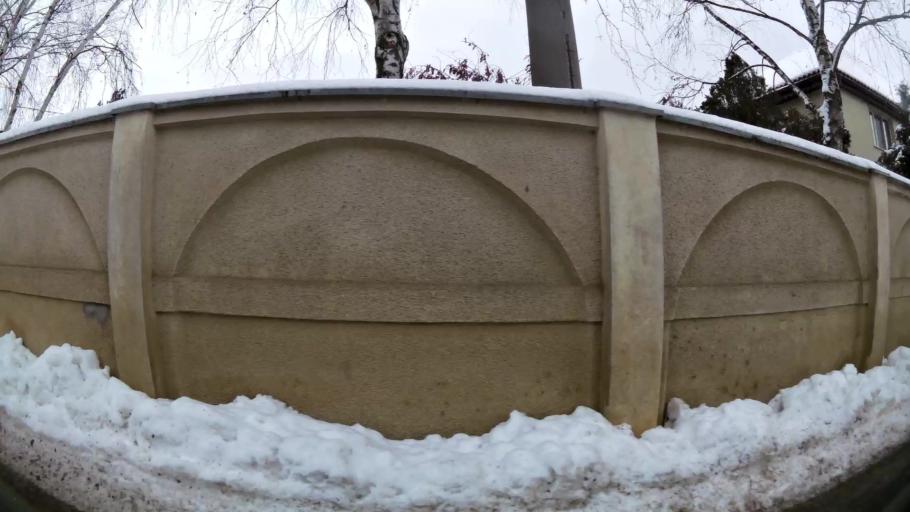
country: RO
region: Ilfov
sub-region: Comuna Otopeni
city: Otopeni
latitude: 44.5135
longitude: 26.1038
